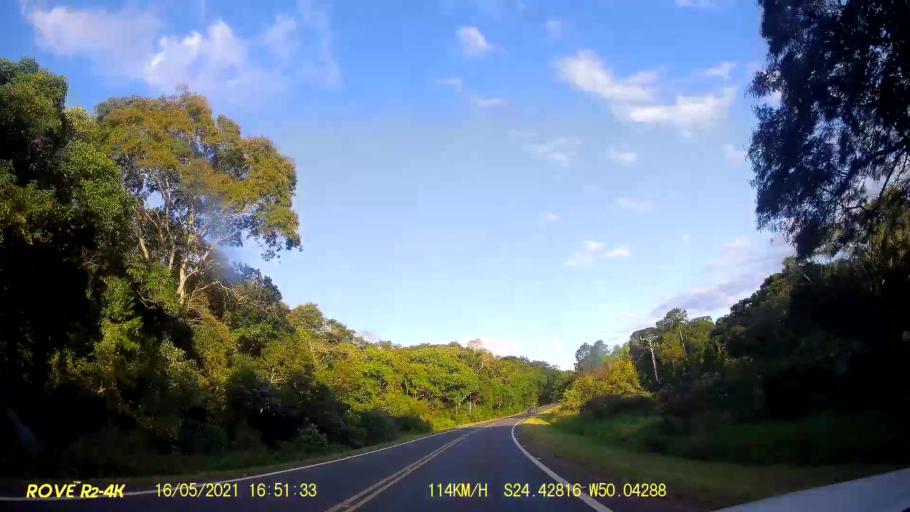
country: BR
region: Parana
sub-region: Pirai Do Sul
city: Pirai do Sul
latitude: -24.4285
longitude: -50.0426
